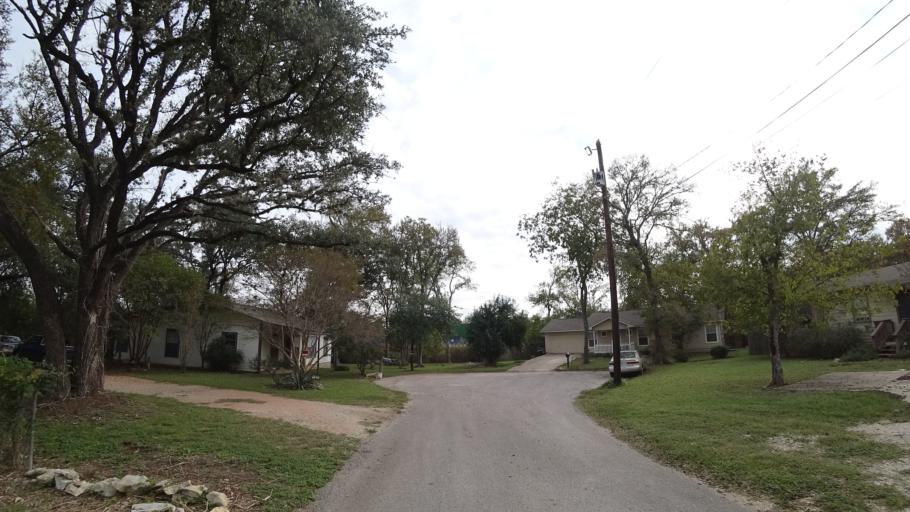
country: US
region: Texas
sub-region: Williamson County
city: Round Rock
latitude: 30.5119
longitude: -97.6639
